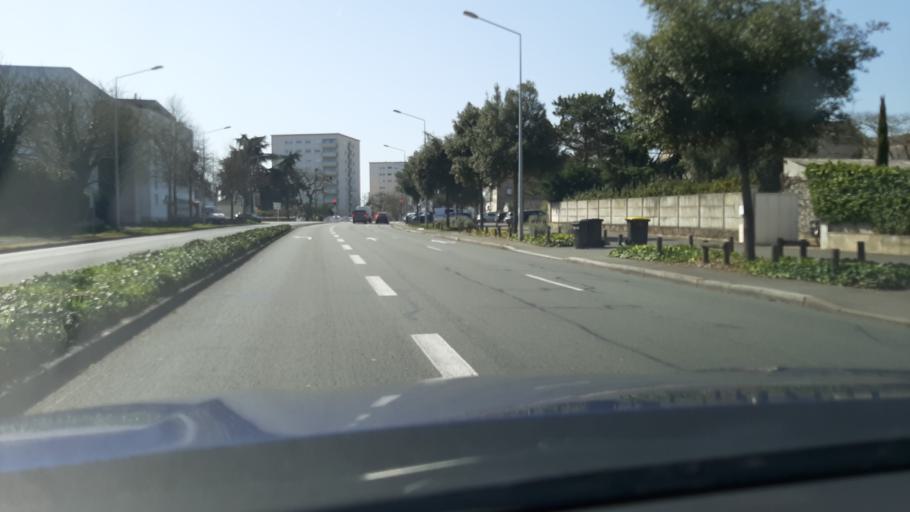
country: FR
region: Pays de la Loire
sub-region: Departement de Maine-et-Loire
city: Angers
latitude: 47.4564
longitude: -0.5287
